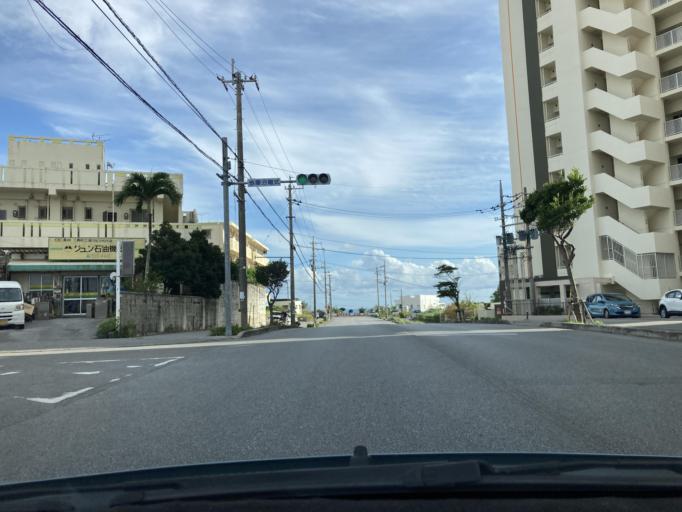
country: JP
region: Okinawa
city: Okinawa
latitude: 26.3395
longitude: 127.8254
